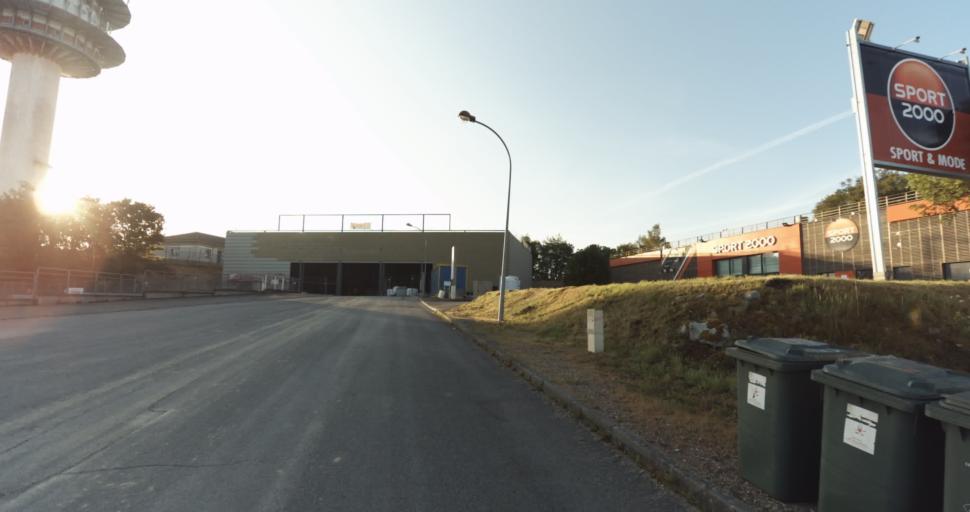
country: FR
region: Limousin
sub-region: Departement de la Haute-Vienne
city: Boisseuil
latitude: 45.7797
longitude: 1.3108
